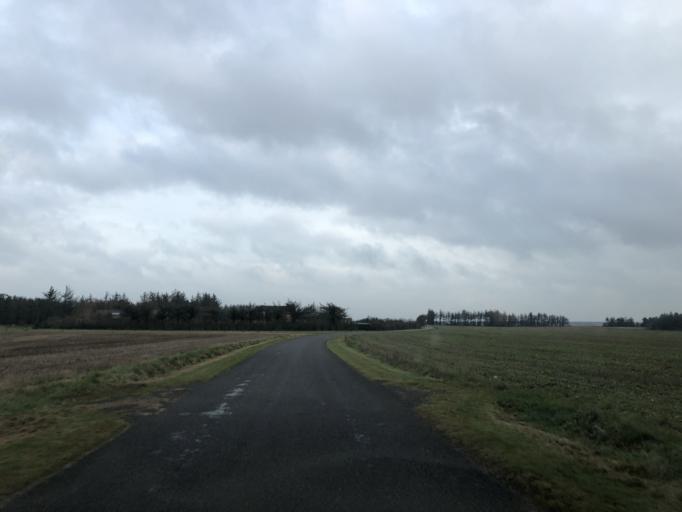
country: DK
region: Central Jutland
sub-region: Holstebro Kommune
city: Ulfborg
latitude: 56.3163
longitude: 8.2203
